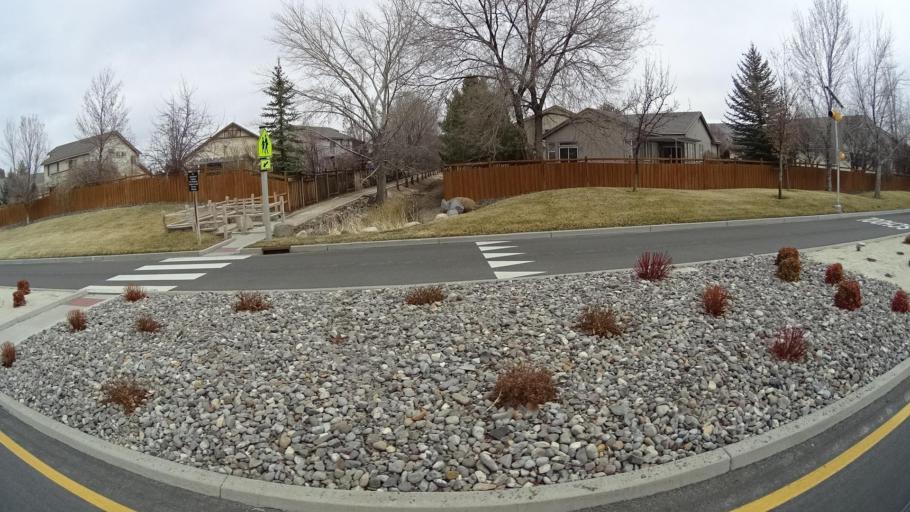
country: US
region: Nevada
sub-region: Washoe County
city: Spanish Springs
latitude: 39.6232
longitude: -119.6850
